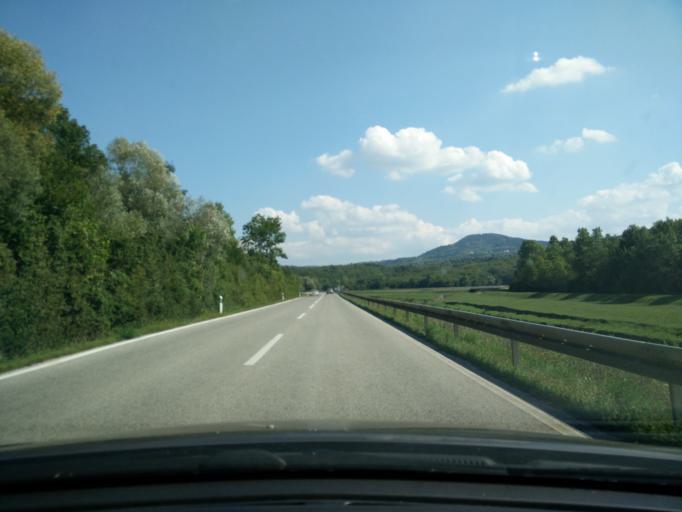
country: HR
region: Istarska
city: Karojba
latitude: 45.3458
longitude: 13.7852
